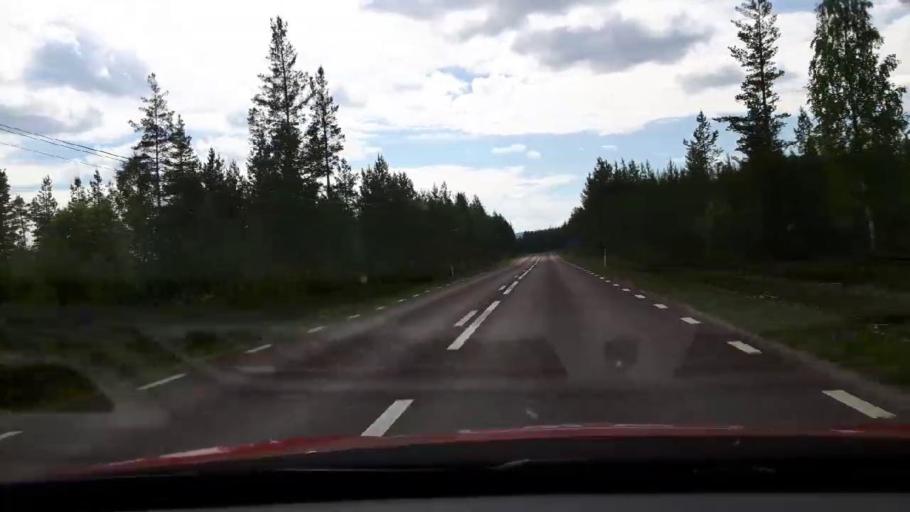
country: SE
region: Jaemtland
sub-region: Harjedalens Kommun
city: Sveg
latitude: 62.1227
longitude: 14.9707
